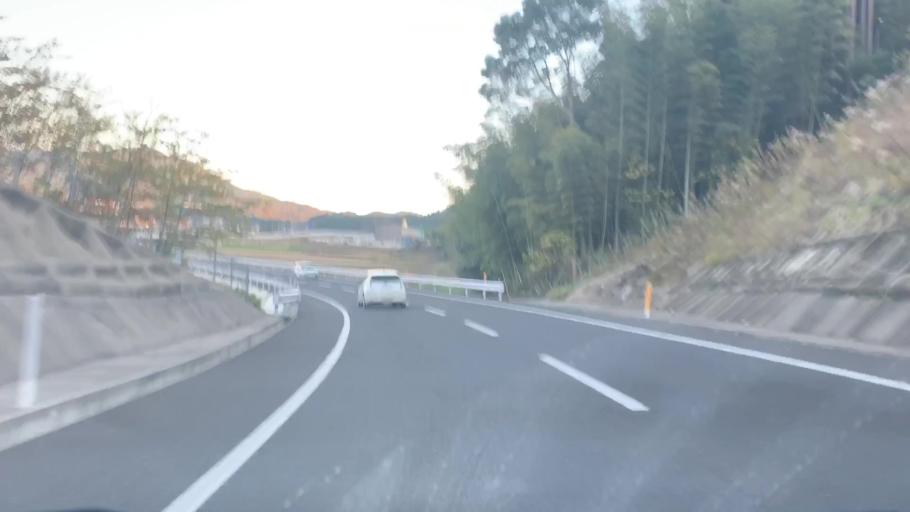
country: JP
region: Saga Prefecture
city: Takeocho-takeo
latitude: 33.2553
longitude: 129.9828
